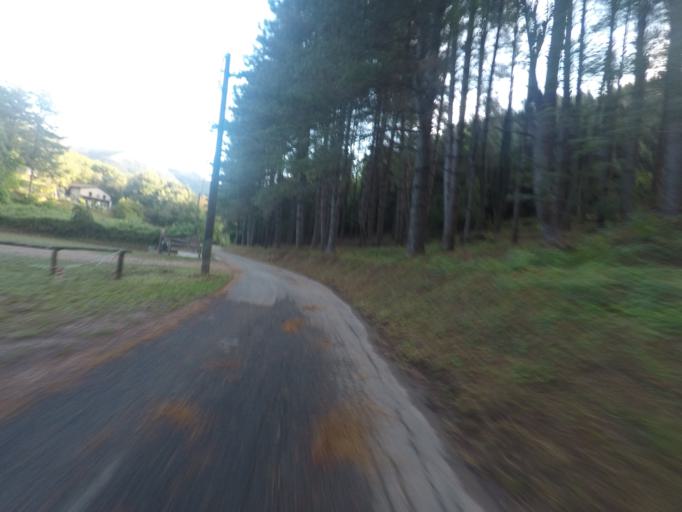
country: IT
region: Tuscany
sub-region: Provincia di Lucca
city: Pescaglia
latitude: 43.9370
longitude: 10.3826
